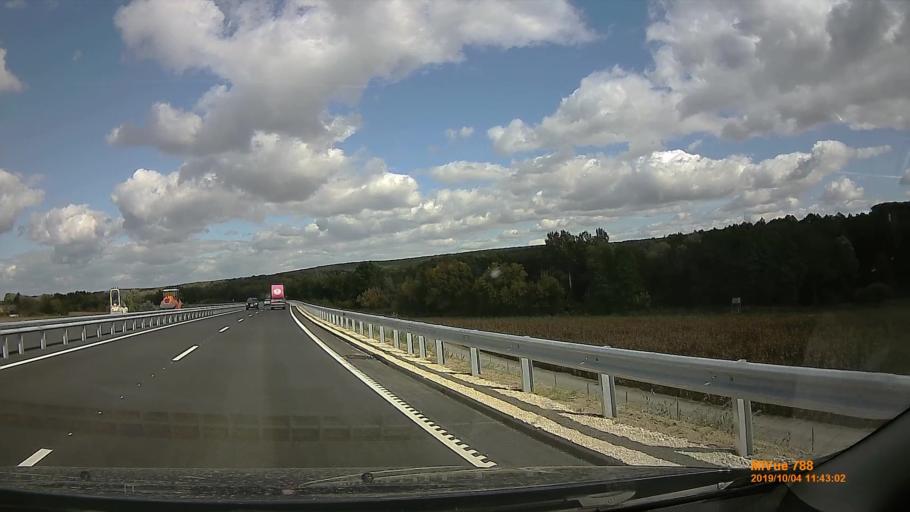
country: HU
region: Somogy
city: Karad
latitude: 46.5963
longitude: 17.8026
